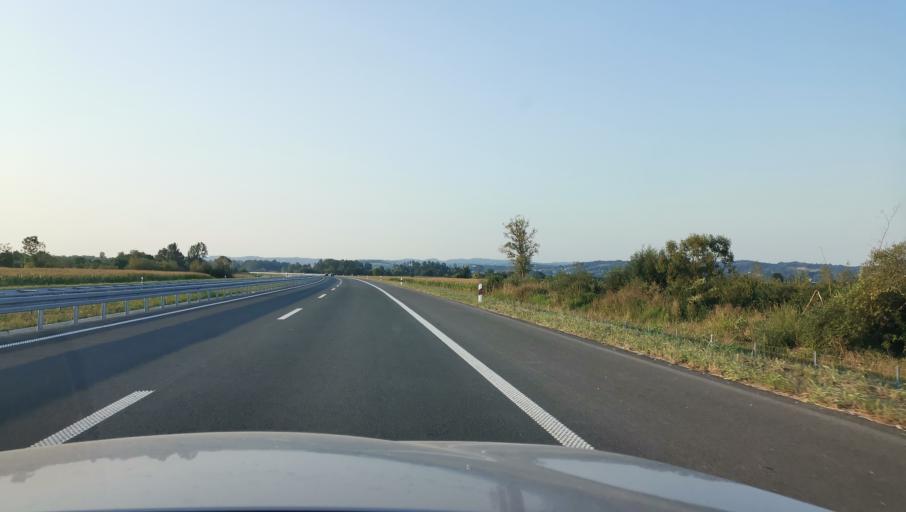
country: RS
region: Central Serbia
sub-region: Kolubarski Okrug
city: Ljig
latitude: 44.2577
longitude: 20.2710
